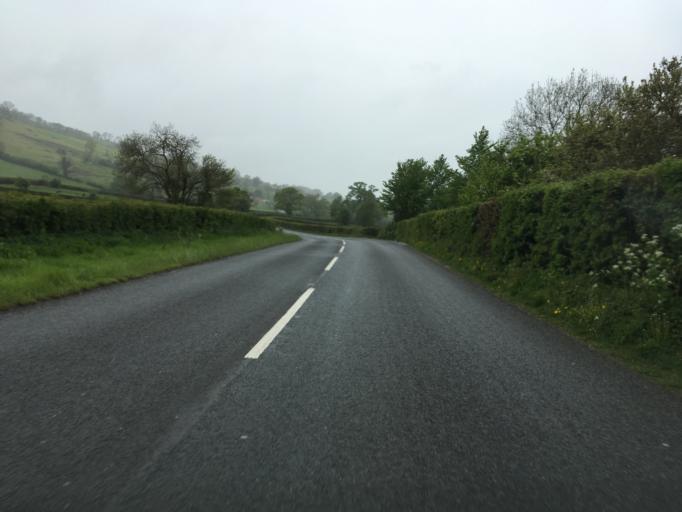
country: GB
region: England
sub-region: Bath and North East Somerset
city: Compton Martin
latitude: 51.3196
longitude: -2.6820
